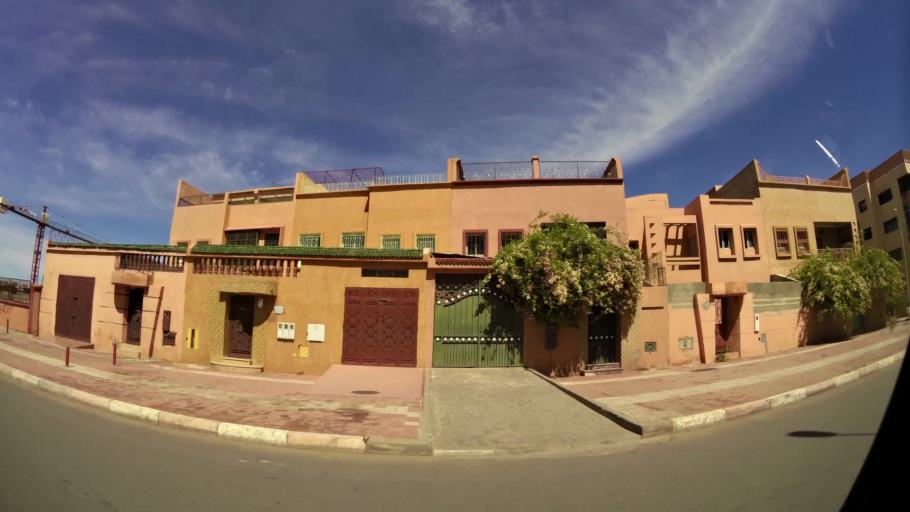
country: MA
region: Marrakech-Tensift-Al Haouz
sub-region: Marrakech
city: Marrakesh
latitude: 31.6054
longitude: -7.9661
